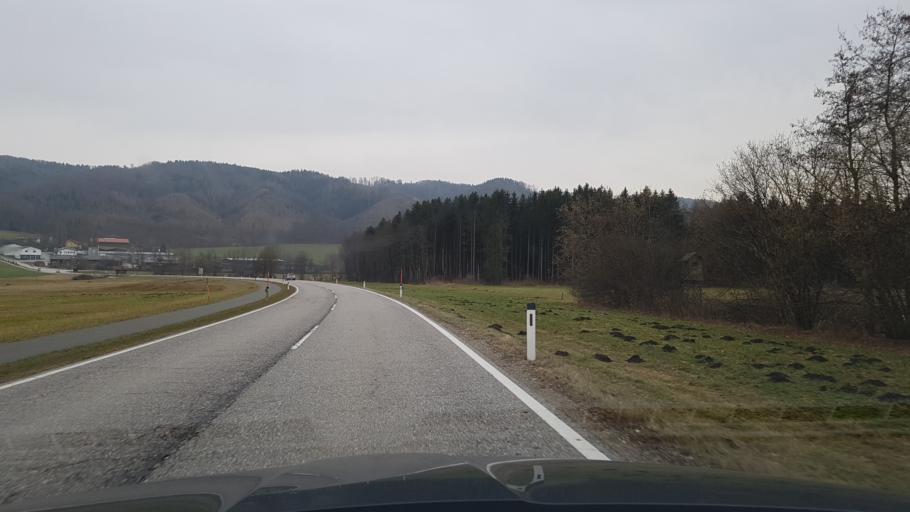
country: AT
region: Salzburg
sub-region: Politischer Bezirk Salzburg-Umgebung
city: Dorfbeuern
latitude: 48.0063
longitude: 13.0290
